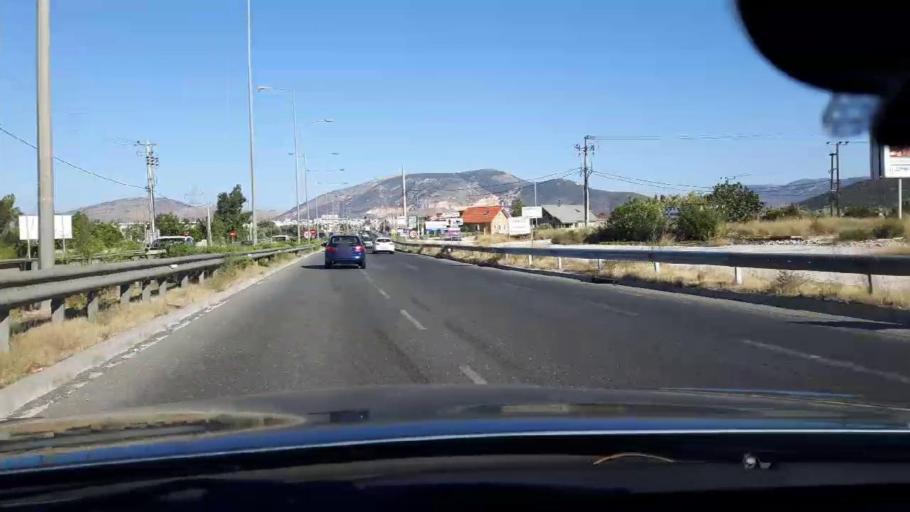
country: GR
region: Attica
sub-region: Nomarchia Anatolikis Attikis
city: Markopoulo
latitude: 37.8920
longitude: 23.9178
